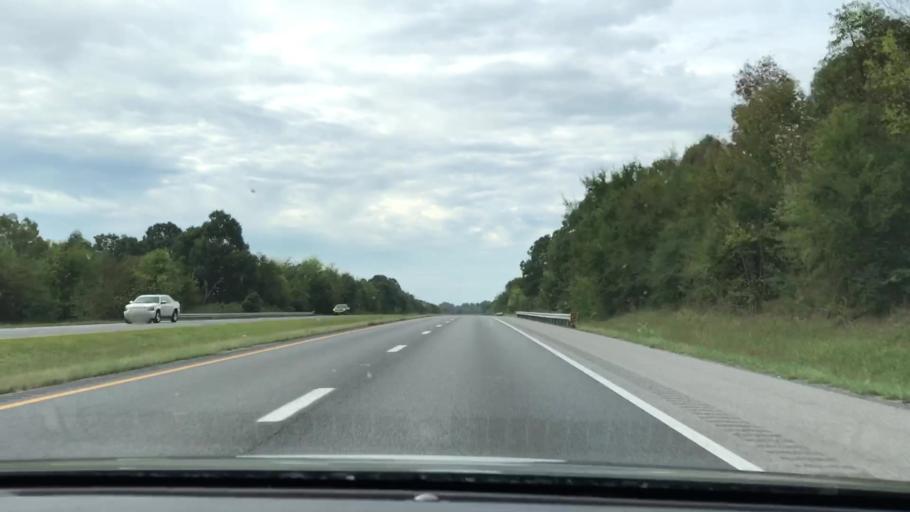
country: US
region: Kentucky
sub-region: Marshall County
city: Calvert City
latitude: 36.9608
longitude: -88.3487
